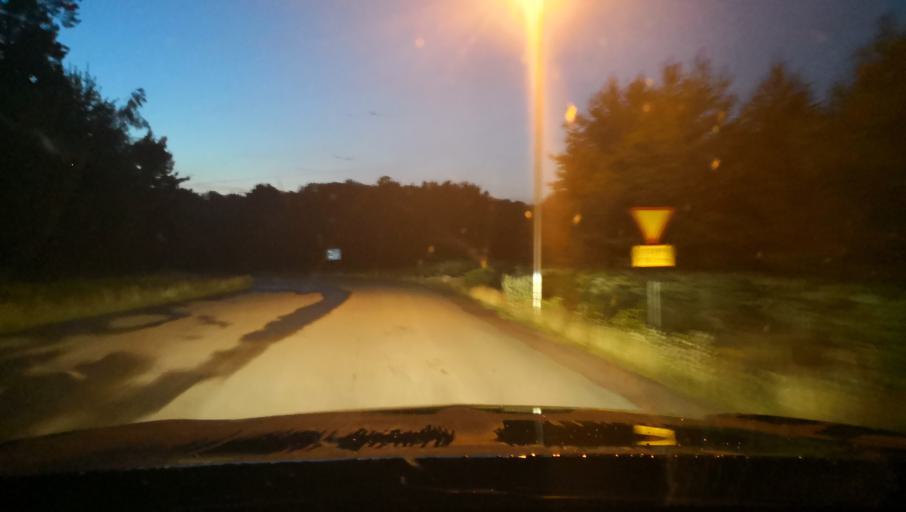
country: SE
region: Skane
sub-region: Hassleholms Kommun
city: Hassleholm
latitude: 56.1702
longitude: 13.8211
